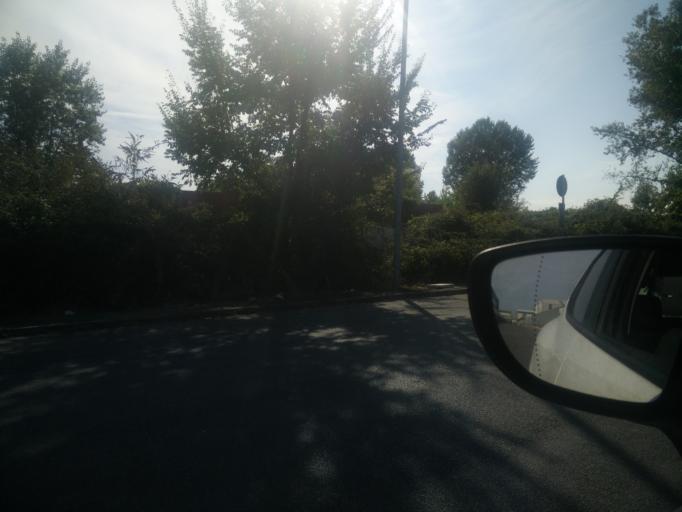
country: IT
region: Tuscany
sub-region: Provincia di Massa-Carrara
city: Massa
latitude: 44.0299
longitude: 10.0961
